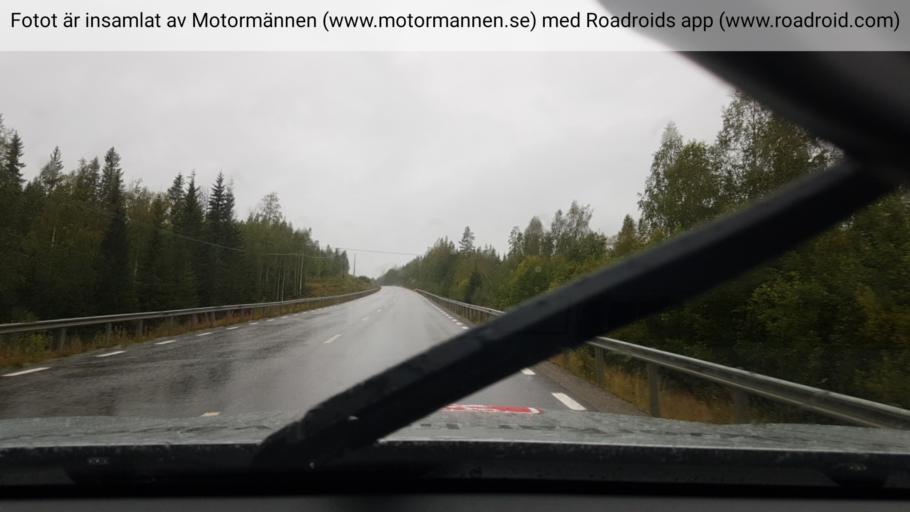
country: SE
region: Vaesterbotten
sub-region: Vannas Kommun
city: Vaennaes
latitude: 63.9267
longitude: 19.5822
